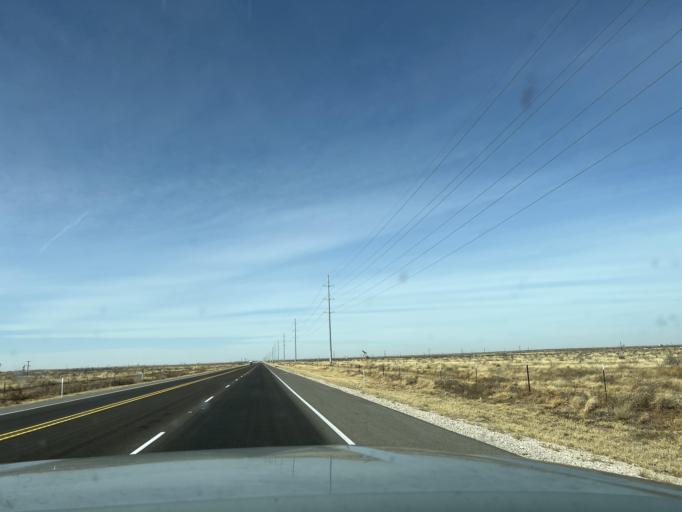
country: US
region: Texas
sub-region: Andrews County
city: Andrews
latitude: 32.3425
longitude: -102.6978
